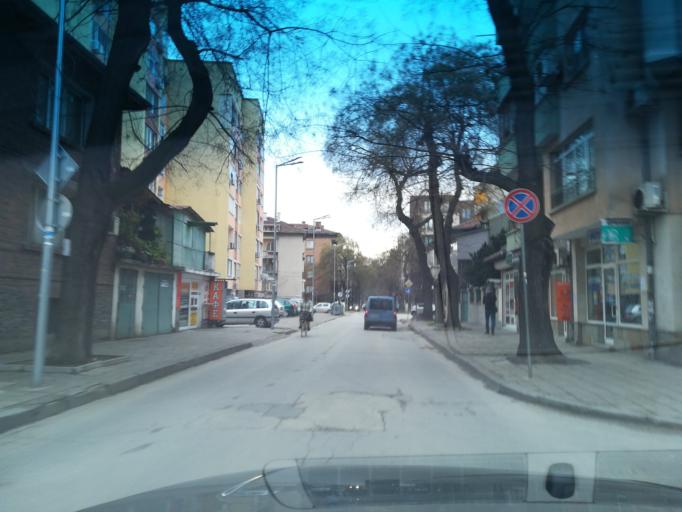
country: BG
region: Plovdiv
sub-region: Obshtina Plovdiv
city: Plovdiv
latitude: 42.1454
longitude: 24.7585
